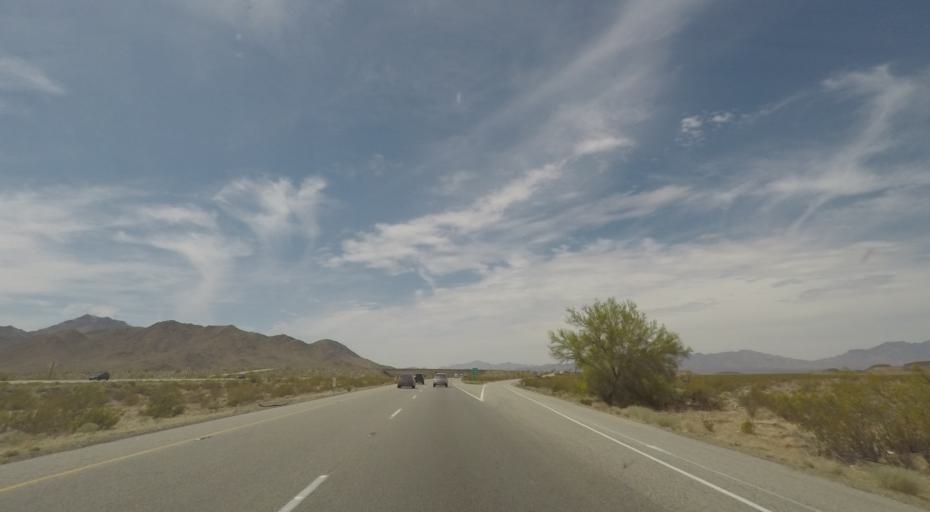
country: US
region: California
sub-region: San Bernardino County
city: Needles
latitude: 34.8016
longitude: -115.3148
